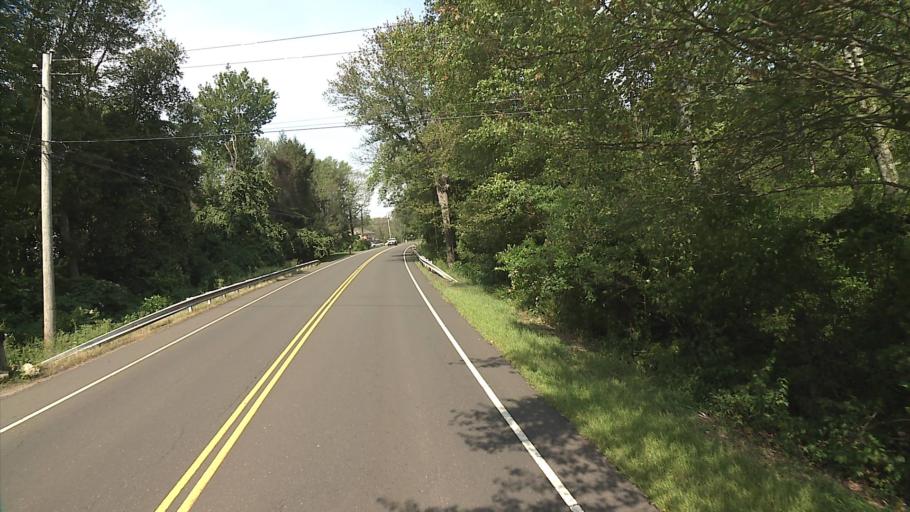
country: US
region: Connecticut
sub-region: Middlesex County
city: Durham
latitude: 41.4434
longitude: -72.6609
